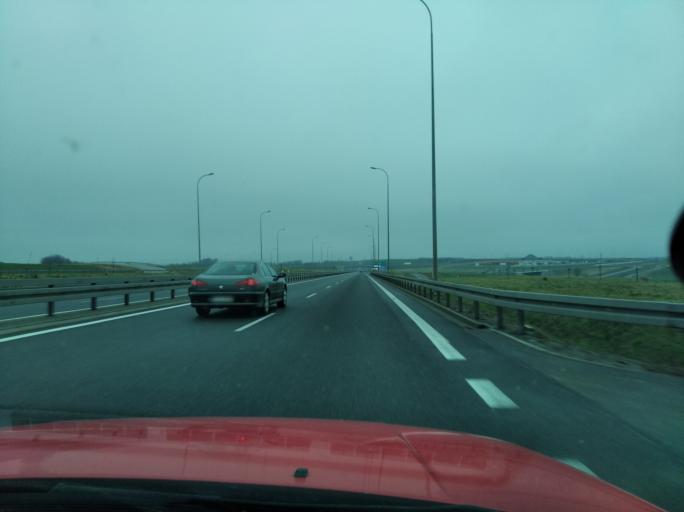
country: PL
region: Subcarpathian Voivodeship
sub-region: Powiat jaroslawski
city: Wierzbna
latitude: 50.0354
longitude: 22.5843
